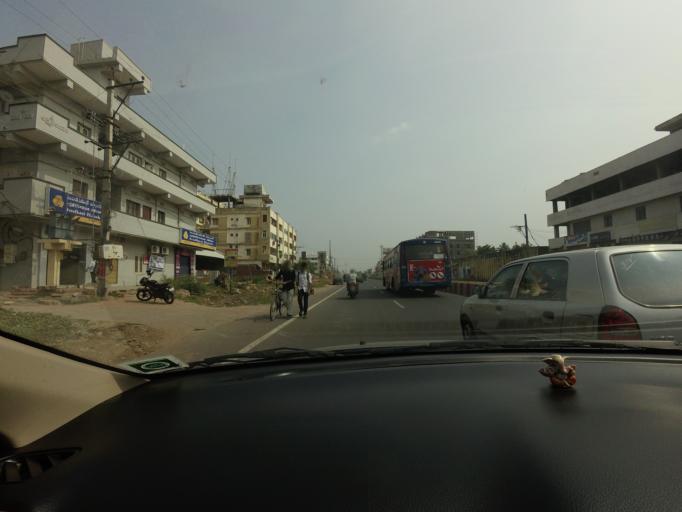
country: IN
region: Andhra Pradesh
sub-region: Krishna
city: Yanamalakuduru
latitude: 16.4835
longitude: 80.6872
